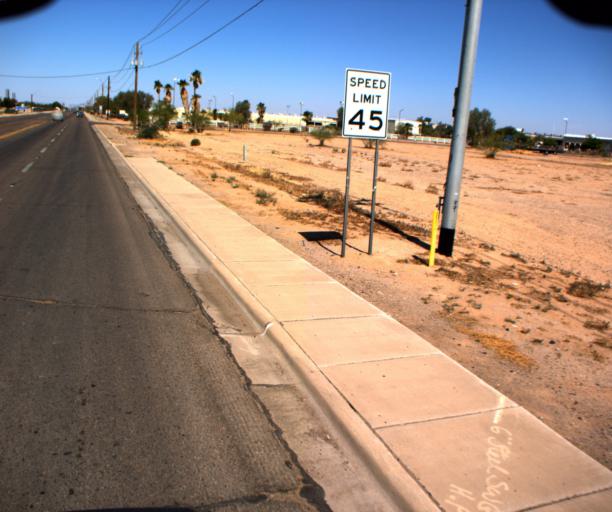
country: US
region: Arizona
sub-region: Pinal County
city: Casa Grande
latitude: 32.8795
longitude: -111.7751
